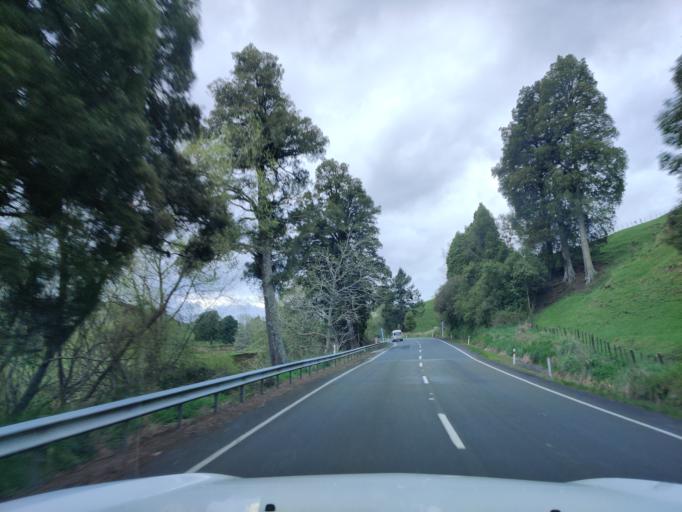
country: NZ
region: Waikato
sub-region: Otorohanga District
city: Otorohanga
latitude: -38.4825
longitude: 175.1747
